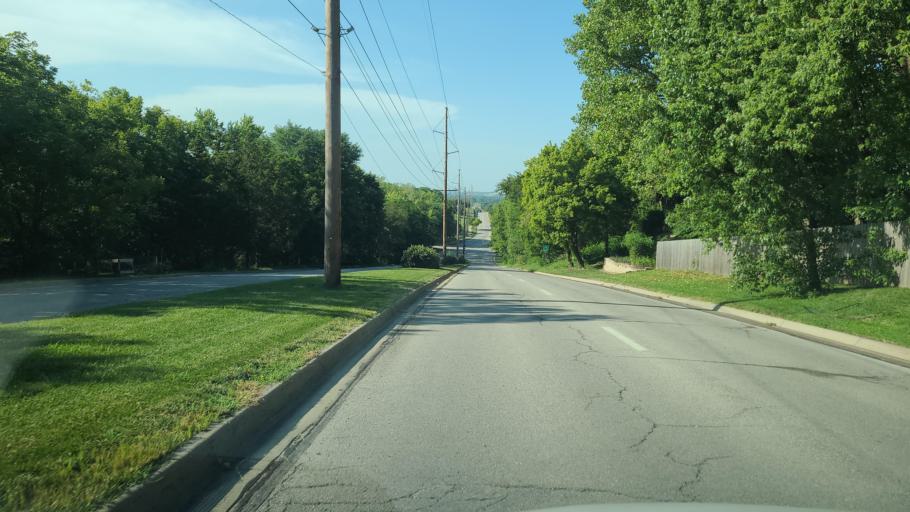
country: US
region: Kansas
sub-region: Douglas County
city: Lawrence
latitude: 38.9790
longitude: -95.2791
